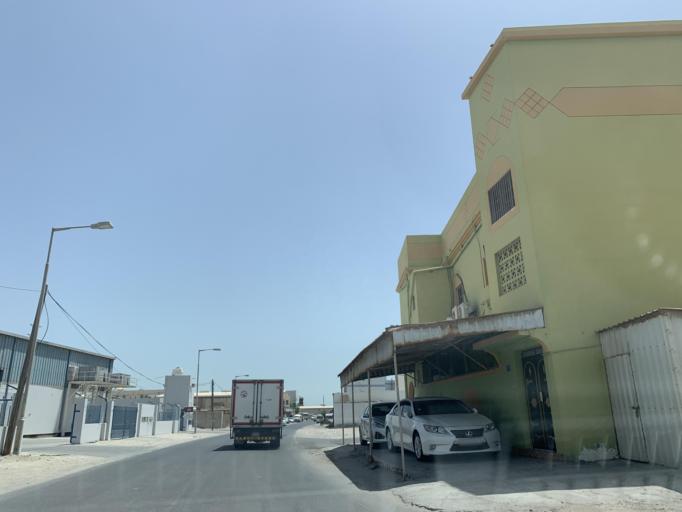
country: BH
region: Northern
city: Sitrah
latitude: 26.1737
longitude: 50.6077
